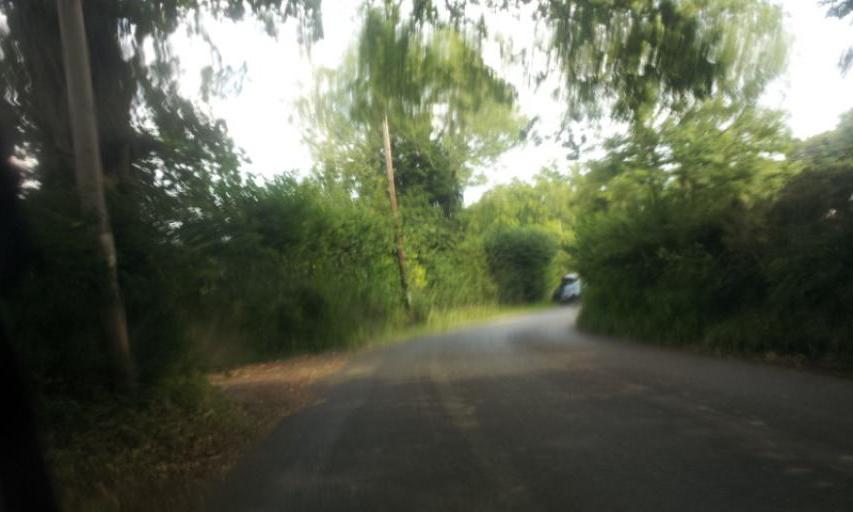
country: GB
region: England
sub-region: Kent
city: Pembury
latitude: 51.1452
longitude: 0.3391
